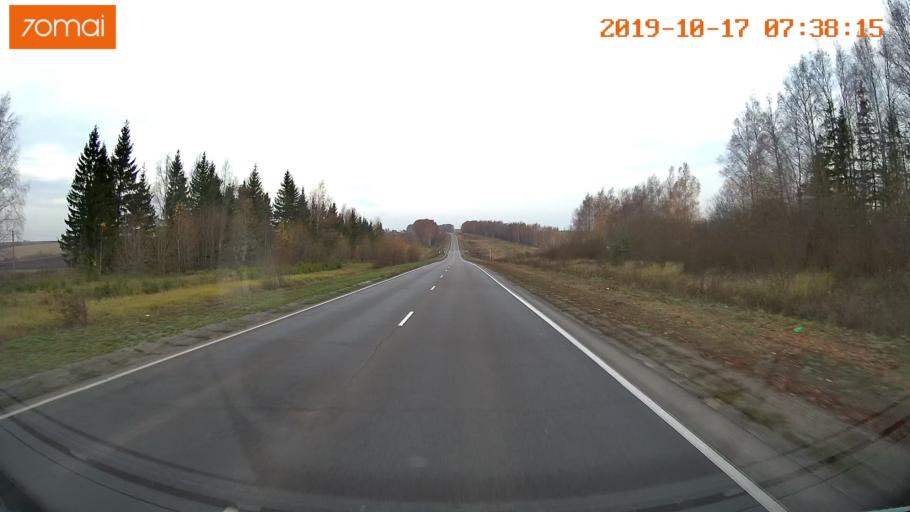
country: RU
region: Vladimir
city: Yur'yev-Pol'skiy
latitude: 56.4542
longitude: 39.8791
